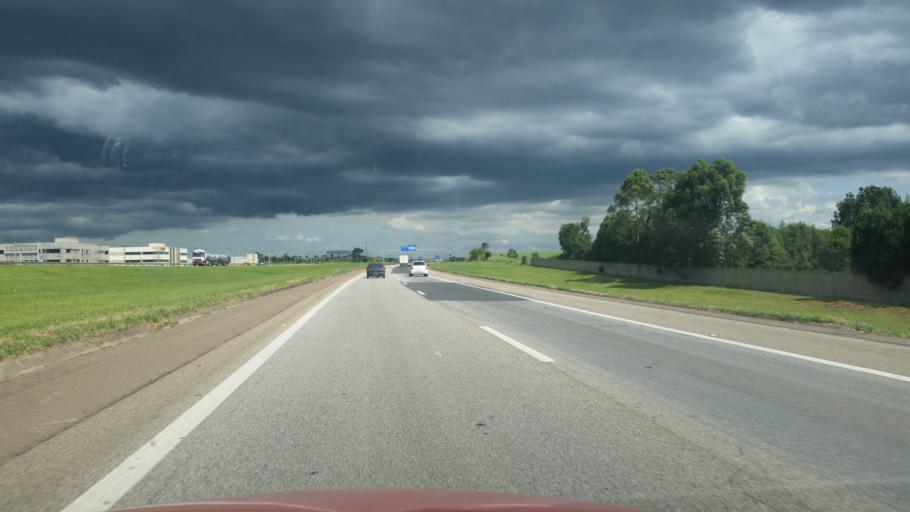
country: BR
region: Sao Paulo
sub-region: Boituva
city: Boituva
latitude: -23.3037
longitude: -47.6594
